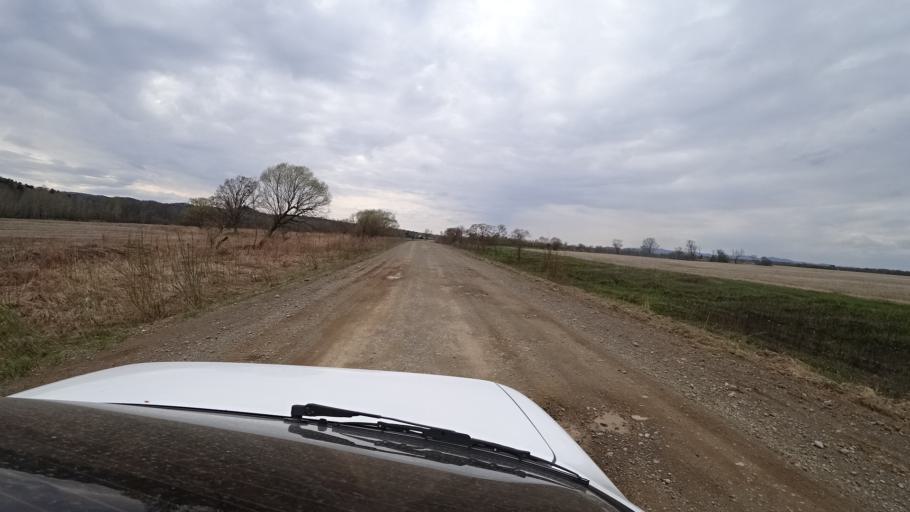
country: RU
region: Primorskiy
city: Novopokrovka
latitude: 45.4895
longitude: 134.4606
